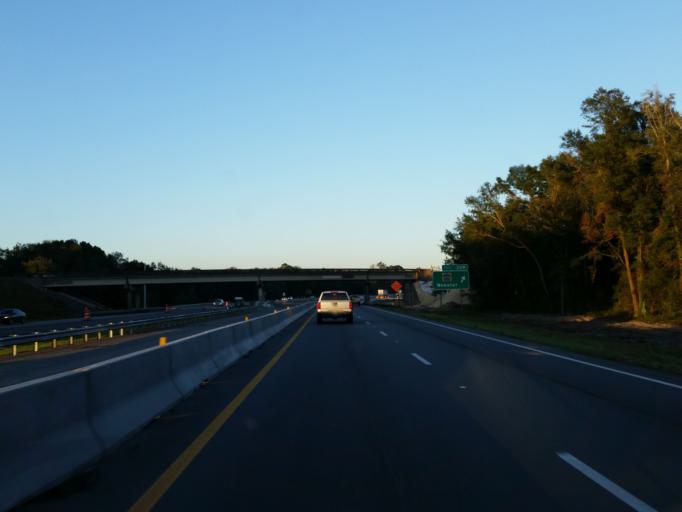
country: US
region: Florida
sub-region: Hernando County
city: Ridge Manor
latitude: 28.6010
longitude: -82.2036
